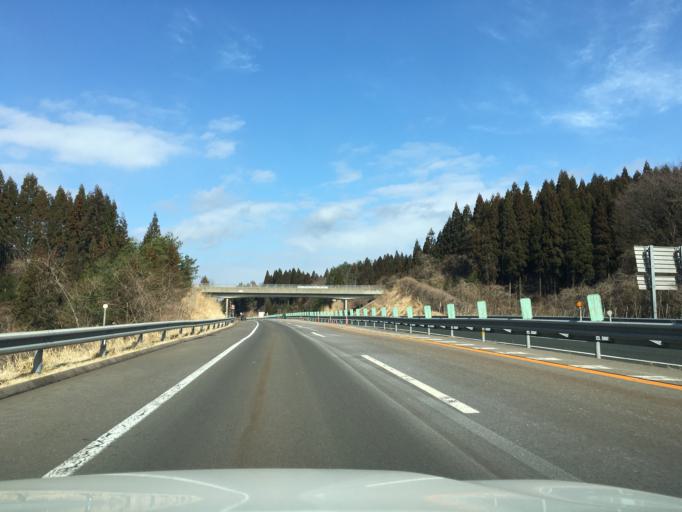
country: JP
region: Akita
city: Akita
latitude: 39.7277
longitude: 140.1802
